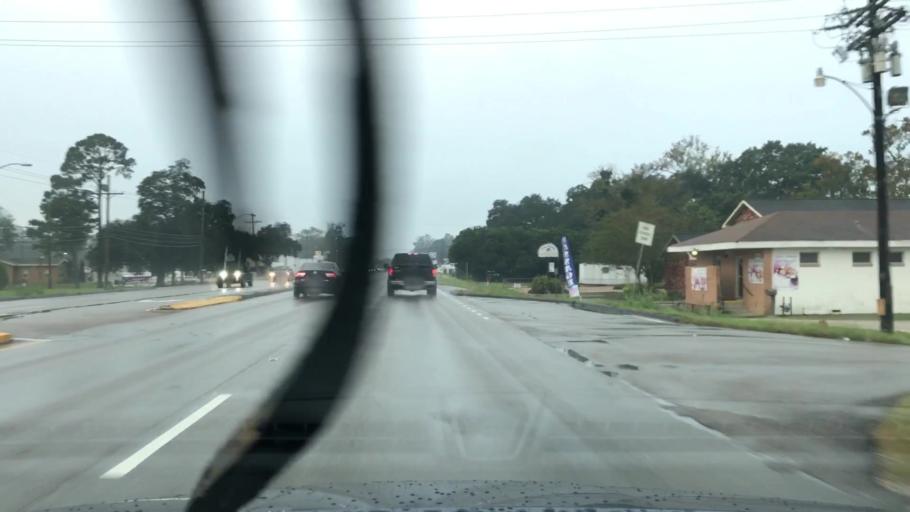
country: US
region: Louisiana
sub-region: Saint Charles Parish
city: Paradis
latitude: 29.8791
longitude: -90.4328
